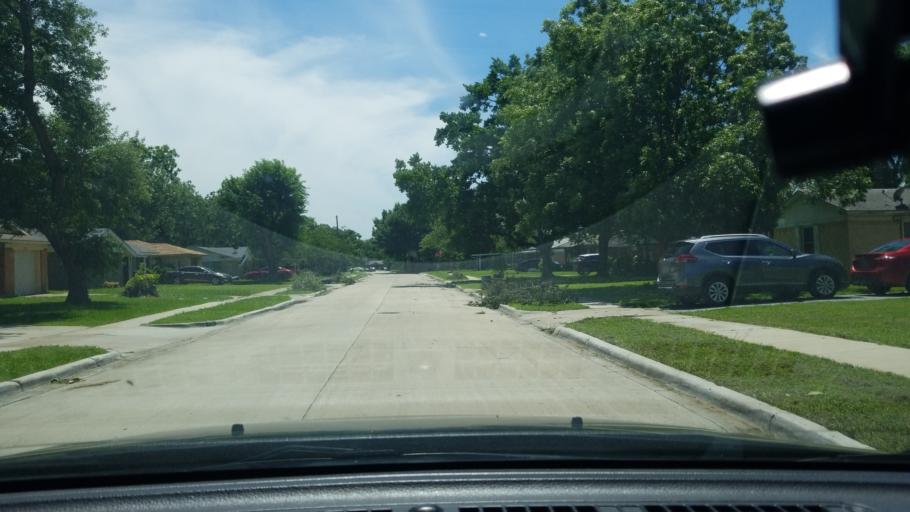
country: US
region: Texas
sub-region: Dallas County
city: Mesquite
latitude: 32.7842
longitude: -96.6201
